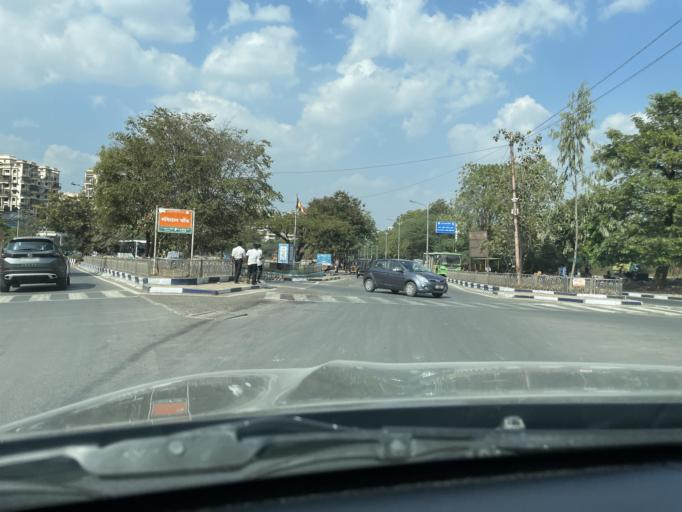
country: IN
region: Maharashtra
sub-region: Pune Division
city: Pune
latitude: 18.4859
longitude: 73.9002
